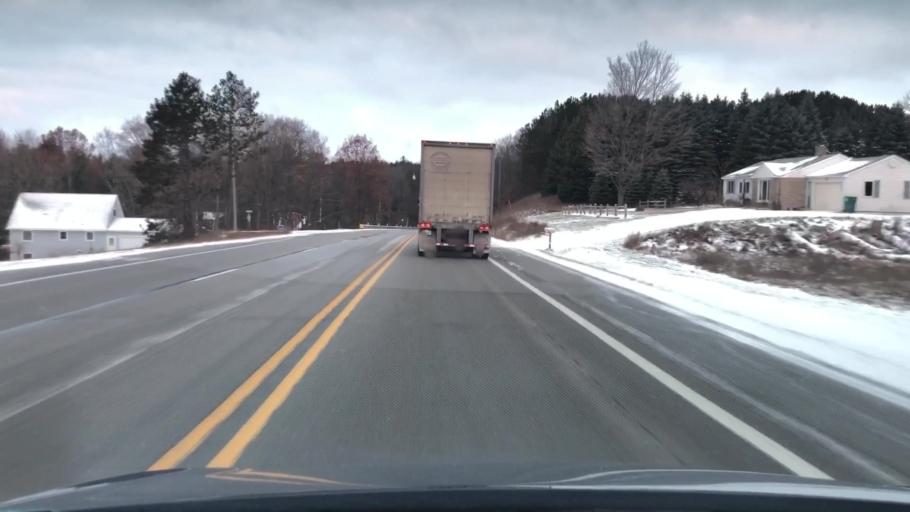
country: US
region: Michigan
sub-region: Wexford County
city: Cadillac
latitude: 44.1822
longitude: -85.3838
